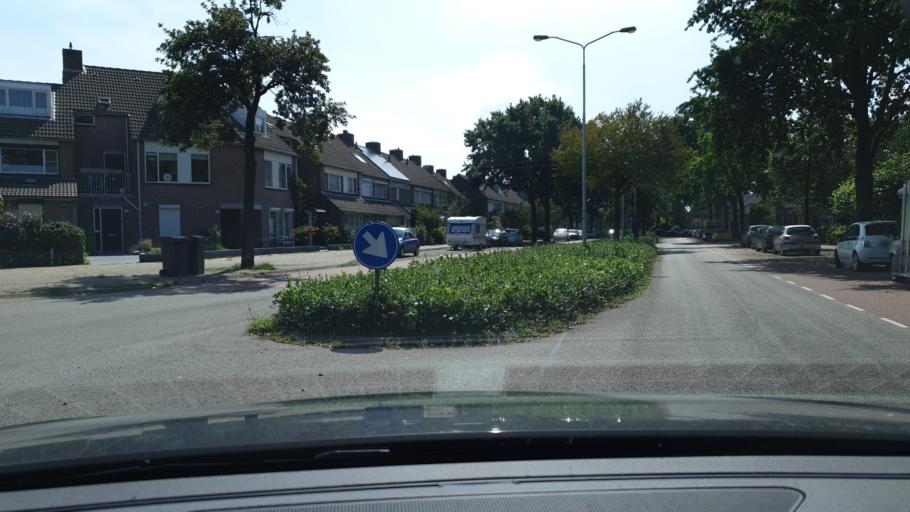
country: NL
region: North Brabant
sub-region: Gemeente Eindhoven
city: Meerhoven
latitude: 51.4836
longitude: 5.4384
